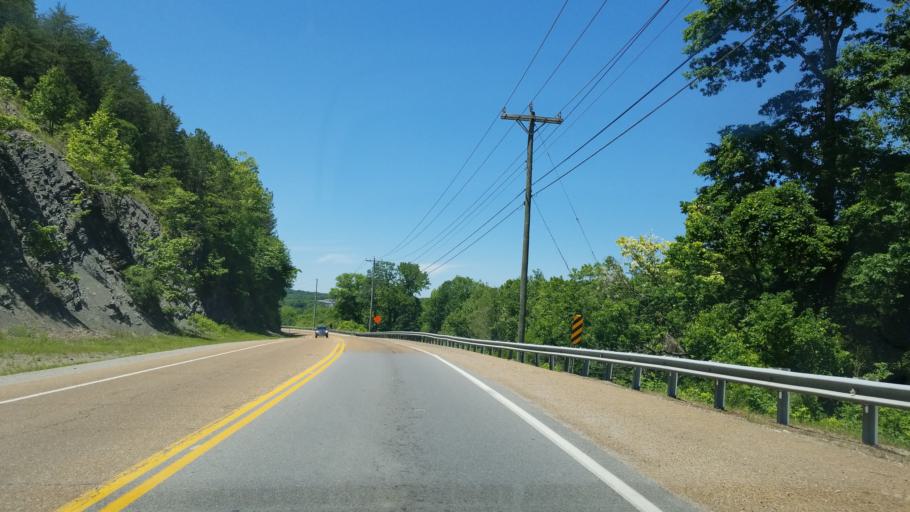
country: US
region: Tennessee
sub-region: Hamilton County
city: Collegedale
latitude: 35.0570
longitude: -85.0574
